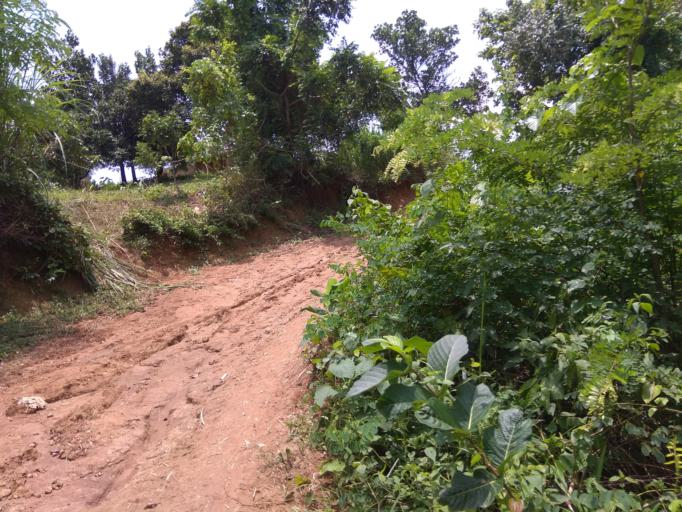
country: BD
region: Chittagong
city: Manikchari
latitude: 22.8856
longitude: 91.9283
